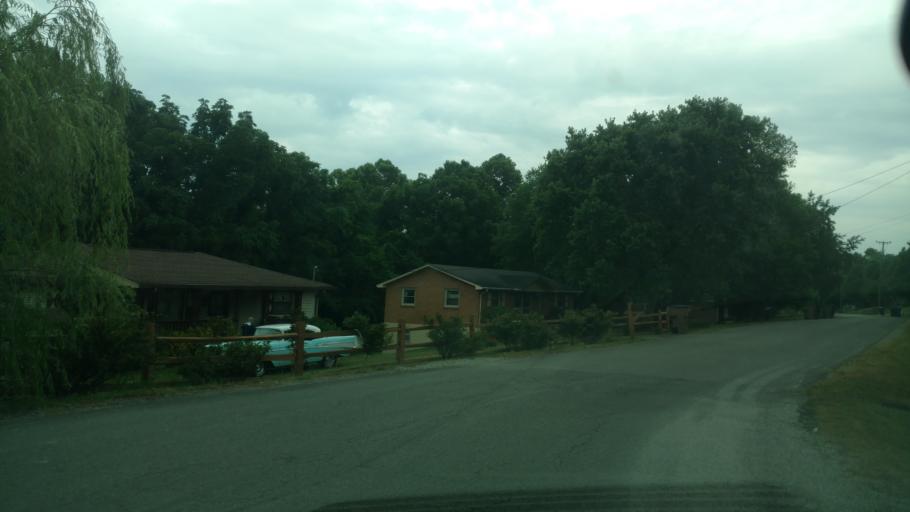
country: US
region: Tennessee
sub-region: Davidson County
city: Nashville
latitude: 36.2018
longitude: -86.7098
